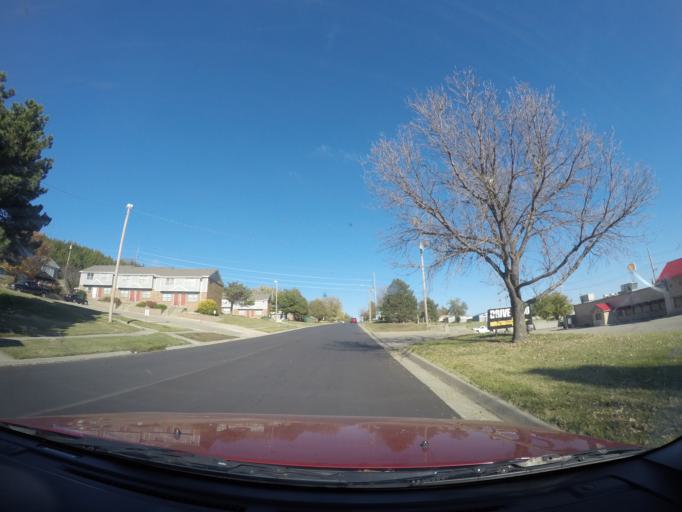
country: US
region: Kansas
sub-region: Geary County
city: Junction City
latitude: 39.0078
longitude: -96.8372
